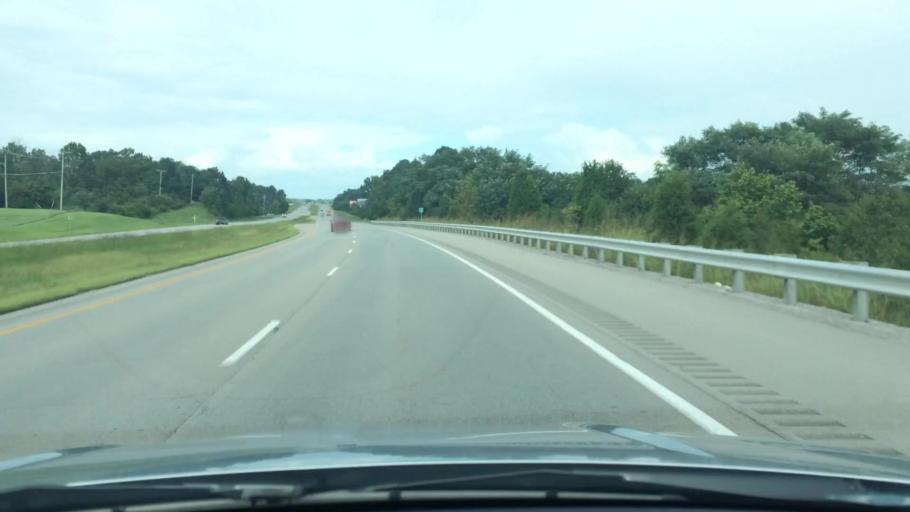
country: US
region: Kentucky
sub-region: Franklin County
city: Frankfort
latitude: 38.1394
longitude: -84.9034
